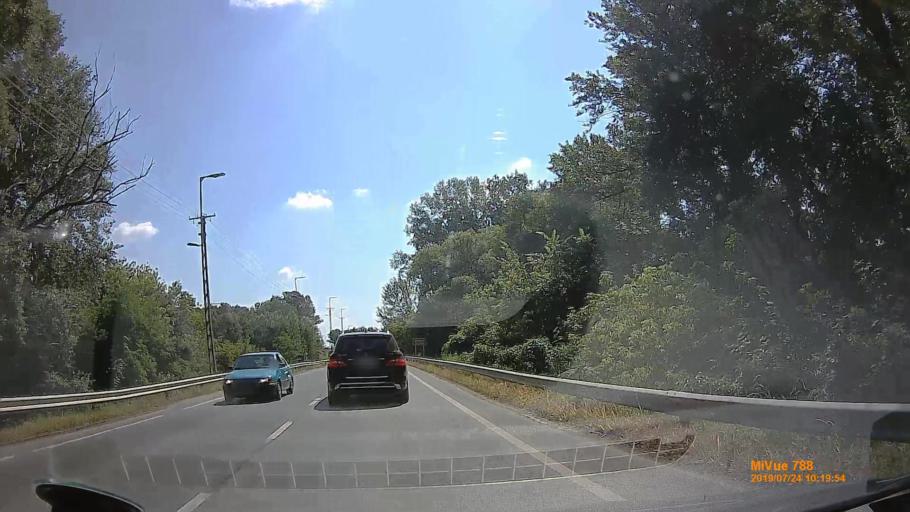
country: HU
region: Szabolcs-Szatmar-Bereg
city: Vasarosnameny
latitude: 48.1264
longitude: 22.3323
